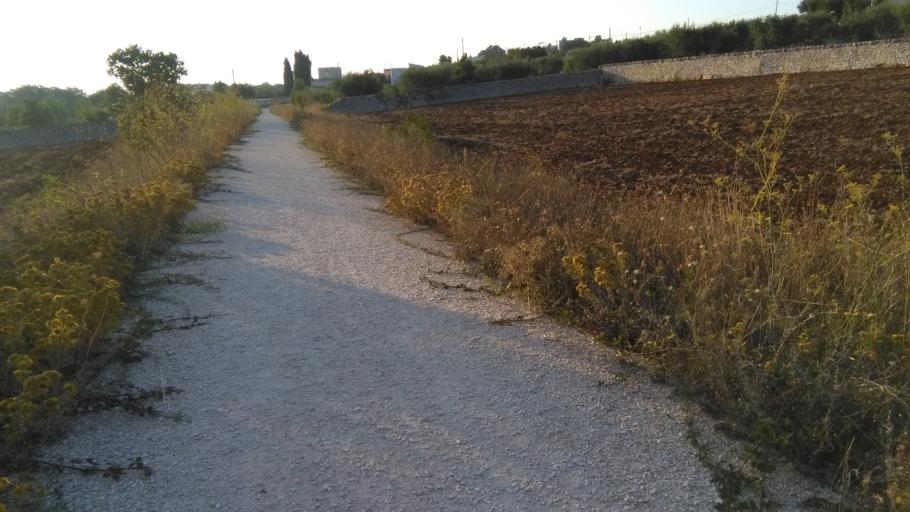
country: IT
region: Apulia
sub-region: Provincia di Brindisi
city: Cisternino
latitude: 40.7425
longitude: 17.3803
